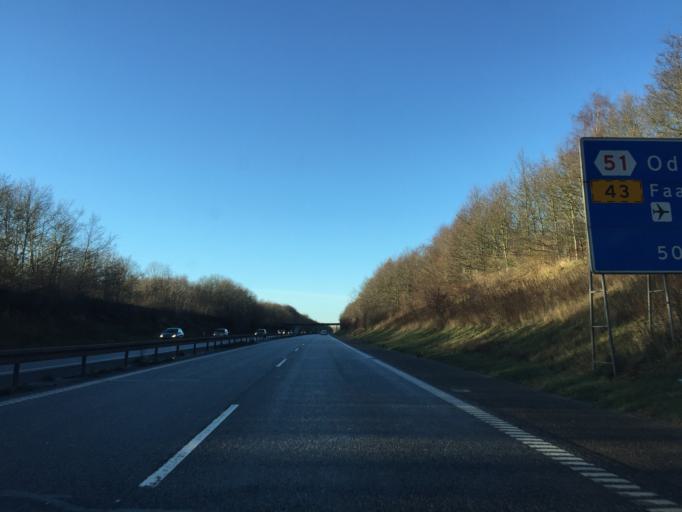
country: DK
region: South Denmark
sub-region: Odense Kommune
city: Hojby
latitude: 55.3518
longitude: 10.3949
